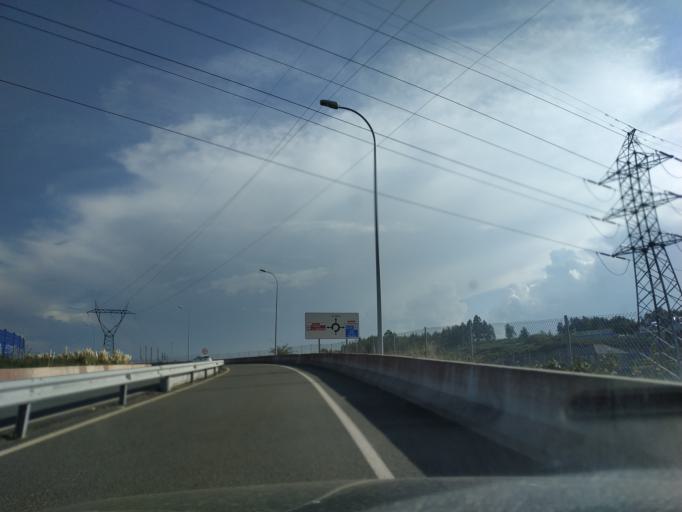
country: ES
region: Galicia
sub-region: Provincia da Coruna
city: Culleredo
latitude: 43.3242
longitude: -8.4099
